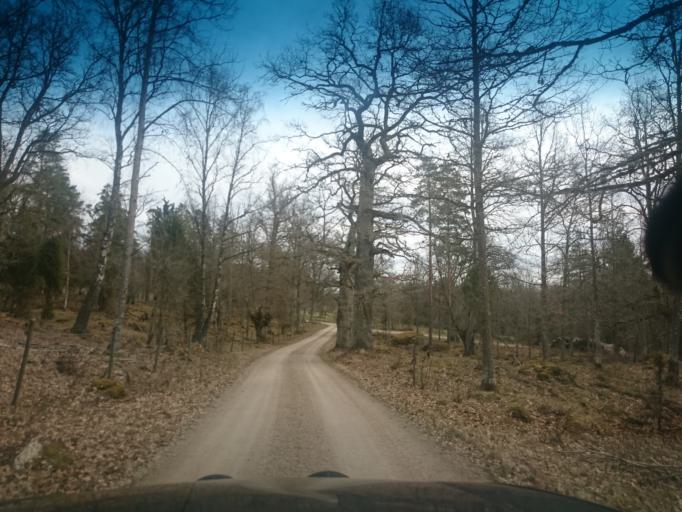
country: SE
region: Joenkoeping
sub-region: Vetlanda Kommun
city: Vetlanda
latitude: 57.3253
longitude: 15.1883
